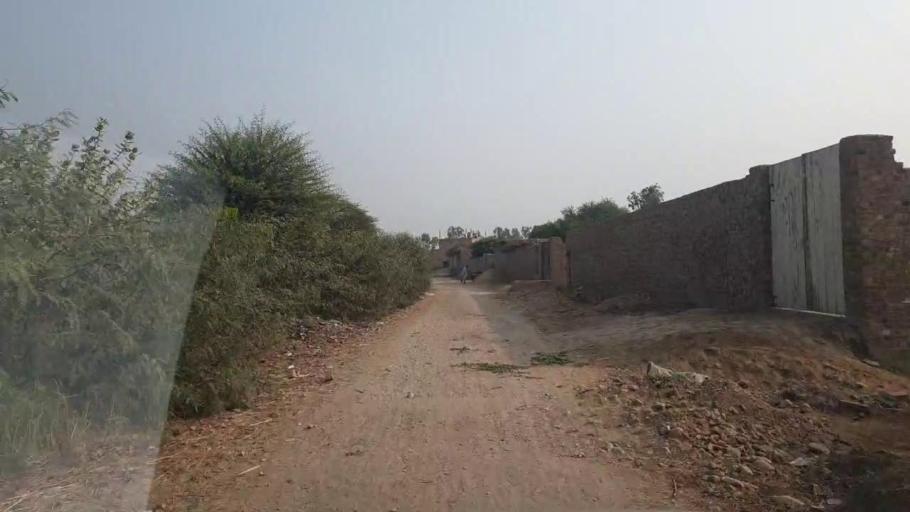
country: PK
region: Sindh
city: Tando Jam
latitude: 25.3383
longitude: 68.5225
